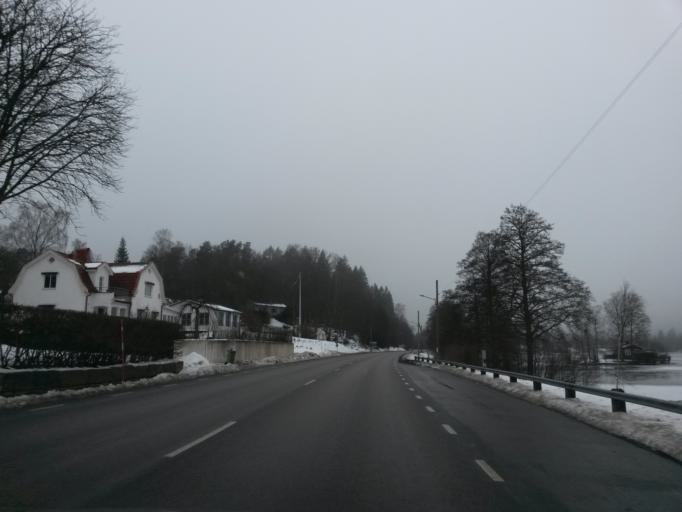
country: SE
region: Vaestra Goetaland
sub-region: Tranemo Kommun
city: Langhem
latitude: 57.6901
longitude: 13.2277
